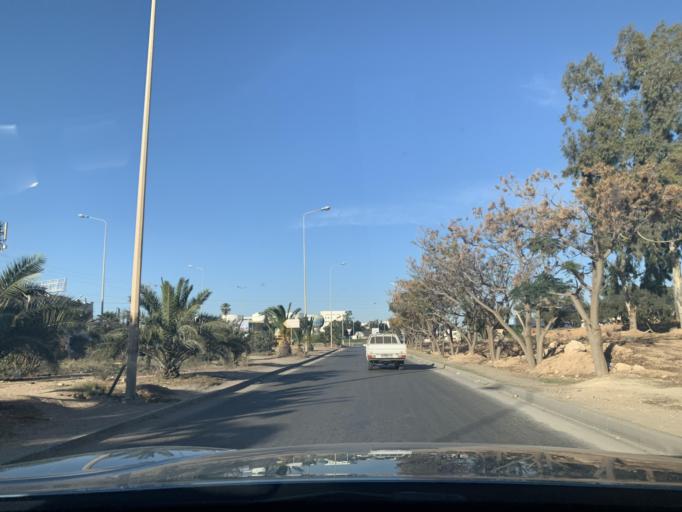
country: DZ
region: Souk Ahras
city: Souk Ahras
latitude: 36.3634
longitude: 8.0077
